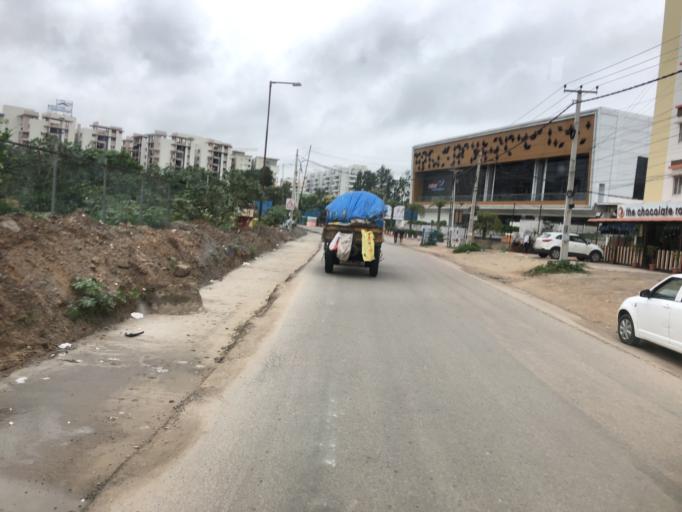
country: IN
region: Telangana
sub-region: Rangareddi
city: Kukatpalli
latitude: 17.4653
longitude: 78.3736
